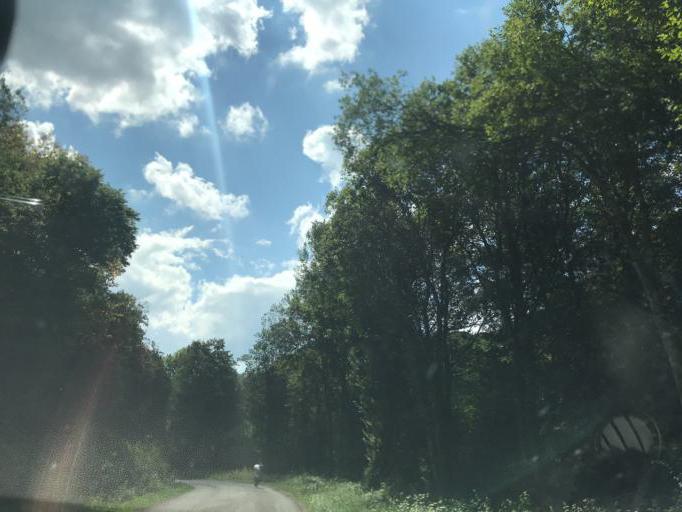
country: FR
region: Franche-Comte
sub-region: Departement du Jura
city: Moirans-en-Montagne
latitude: 46.4899
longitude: 5.7490
